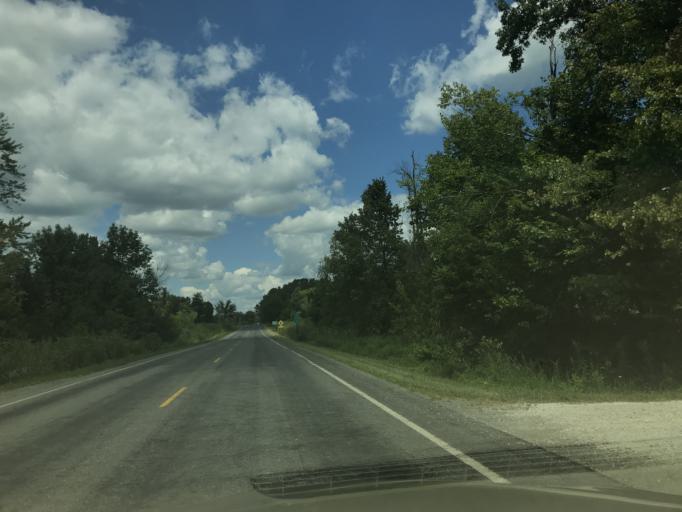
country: US
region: Michigan
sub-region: Eaton County
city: Eaton Rapids
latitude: 42.4633
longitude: -84.5607
